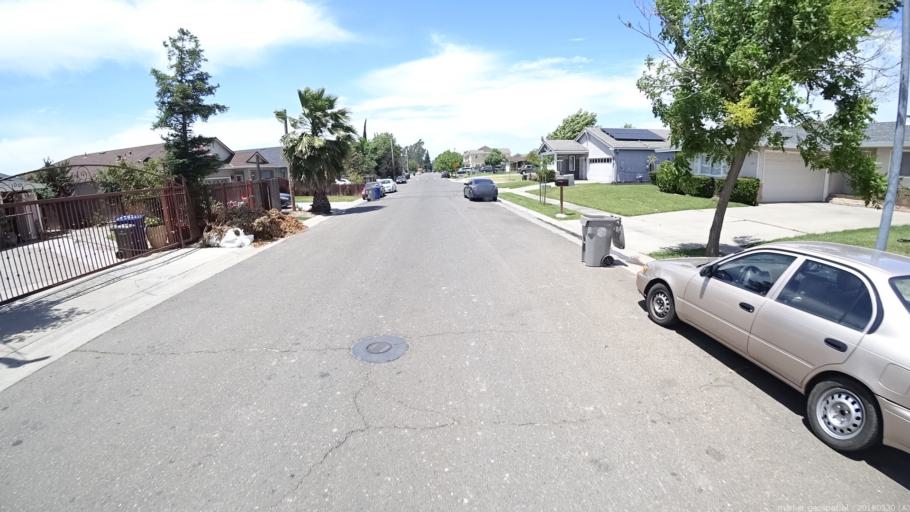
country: US
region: California
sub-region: Sacramento County
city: Sacramento
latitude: 38.6269
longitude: -121.4531
